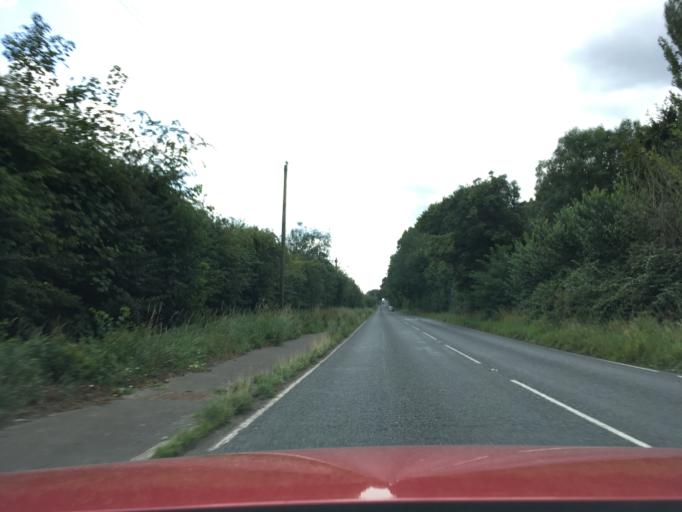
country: GB
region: England
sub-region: Hampshire
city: Kings Worthy
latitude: 51.1097
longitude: -1.2778
